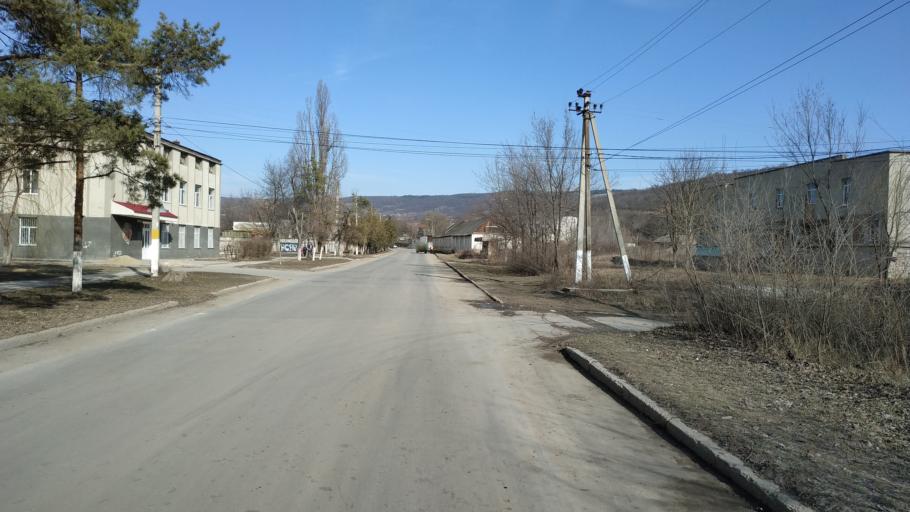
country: MD
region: Nisporeni
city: Nisporeni
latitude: 47.0743
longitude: 28.1814
